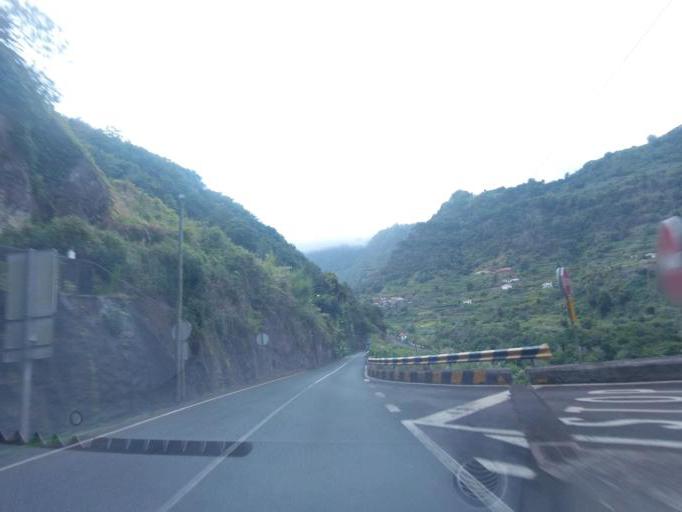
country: PT
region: Madeira
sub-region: Santana
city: Santana
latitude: 32.8144
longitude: -16.8960
